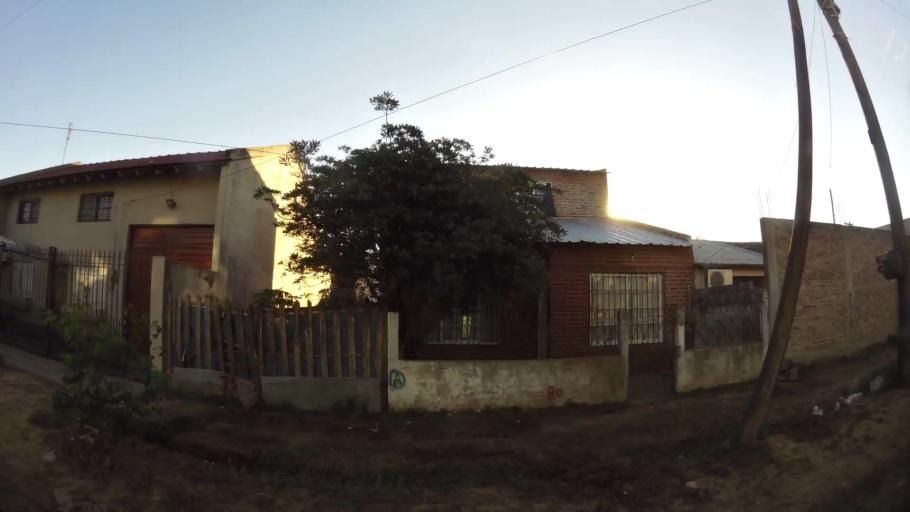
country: AR
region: Buenos Aires
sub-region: Partido de Almirante Brown
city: Adrogue
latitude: -34.7696
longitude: -58.3324
